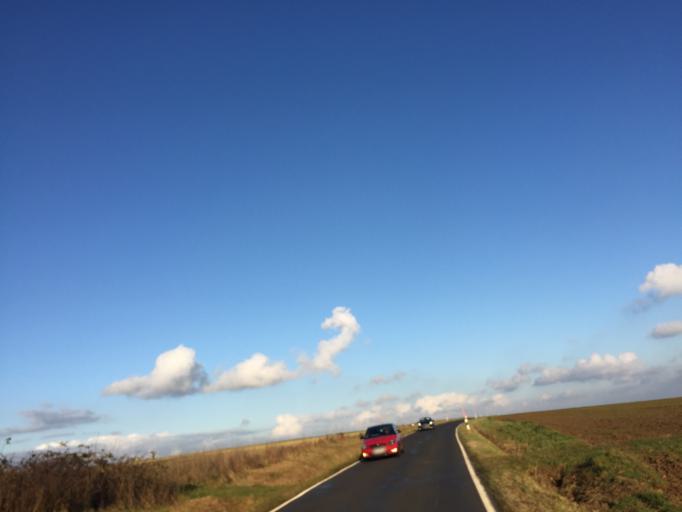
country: DE
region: Hesse
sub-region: Regierungsbezirk Giessen
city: Langgons
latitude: 50.5024
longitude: 8.7046
